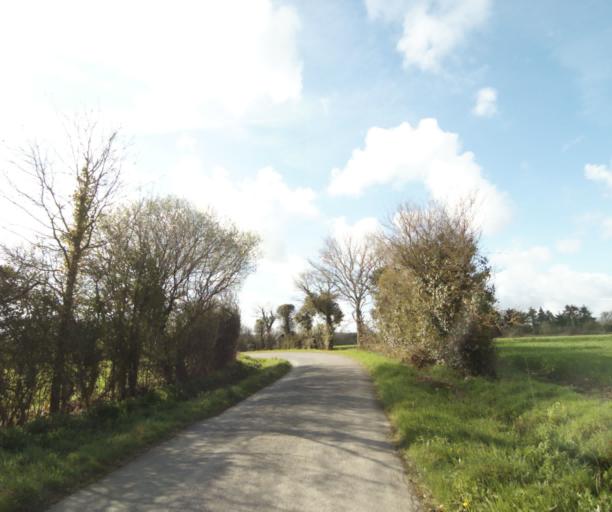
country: FR
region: Pays de la Loire
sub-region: Departement de la Loire-Atlantique
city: Bouvron
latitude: 47.4011
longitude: -1.8360
